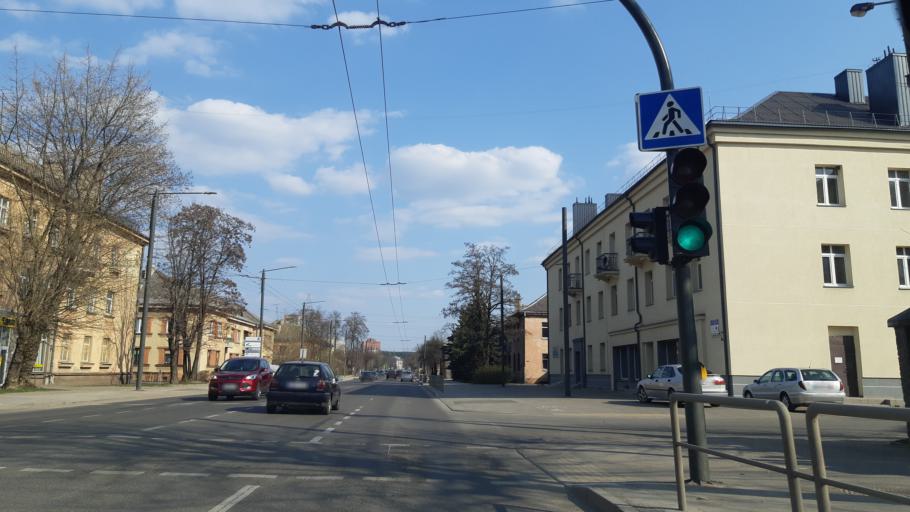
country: LT
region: Kauno apskritis
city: Dainava (Kaunas)
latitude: 54.8944
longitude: 23.9890
